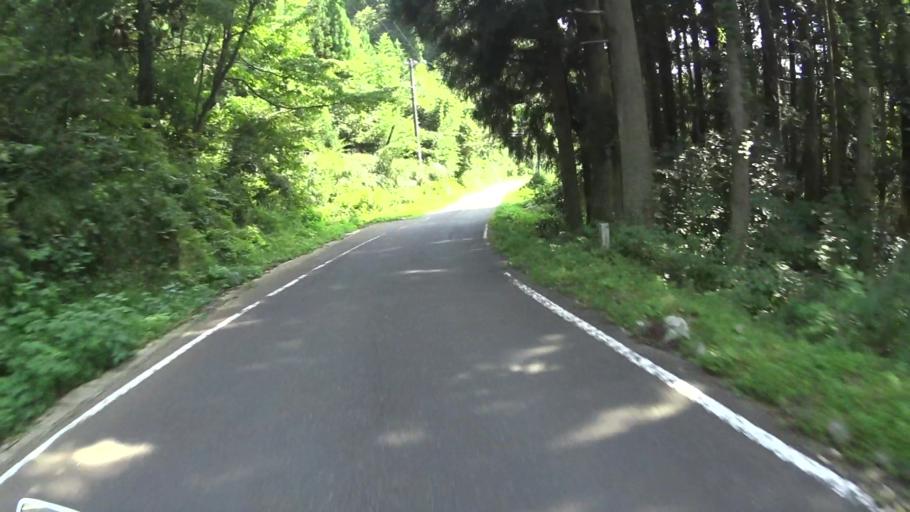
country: JP
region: Kyoto
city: Miyazu
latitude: 35.6356
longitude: 135.1926
